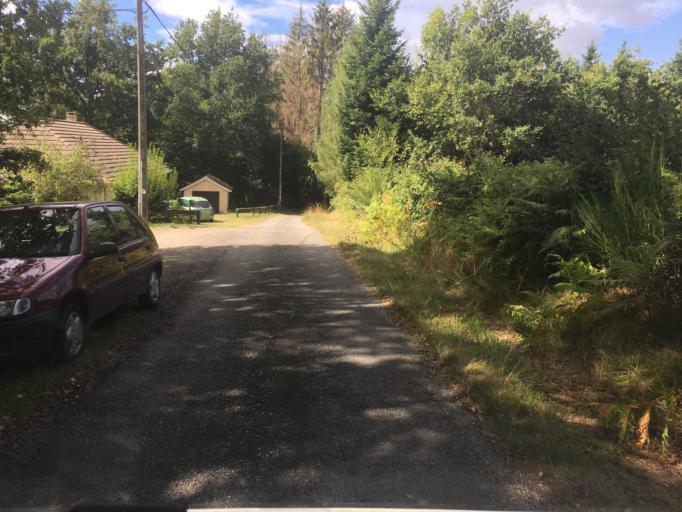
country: FR
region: Auvergne
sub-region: Departement du Cantal
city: Champagnac
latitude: 45.4193
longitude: 2.3831
